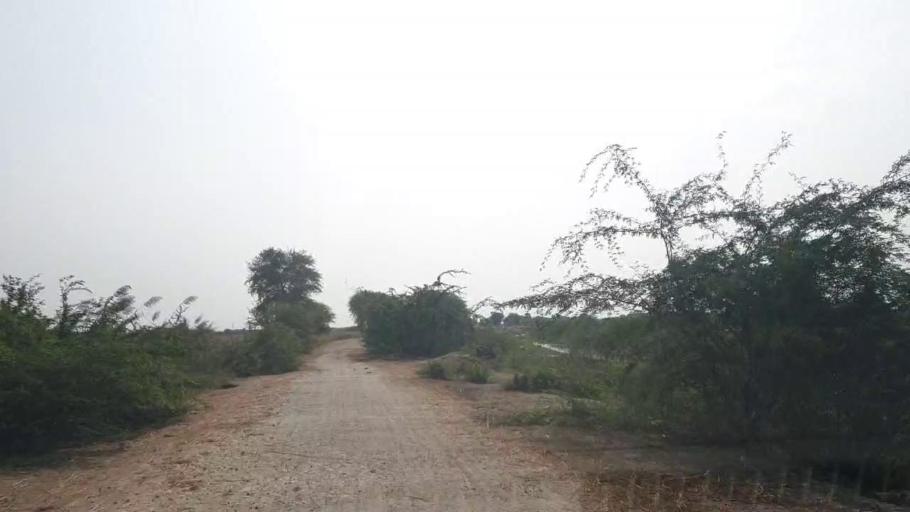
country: PK
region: Sindh
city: Badin
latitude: 24.7587
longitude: 68.7598
